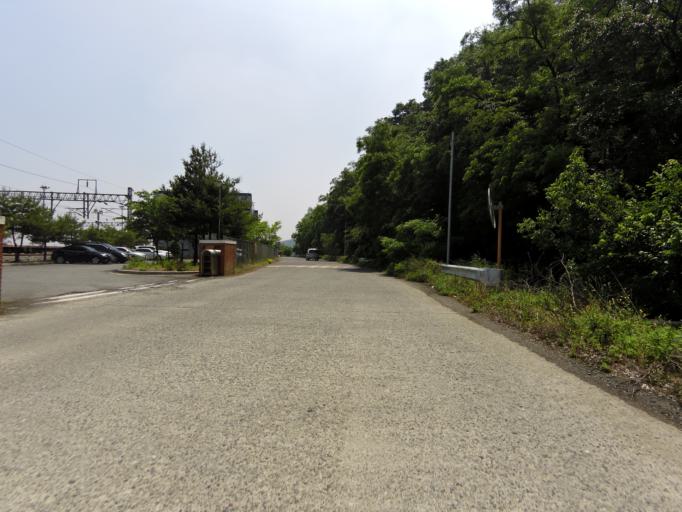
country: KR
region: Gyeongsangbuk-do
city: Gyeongsan-si
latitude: 35.8533
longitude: 128.6918
